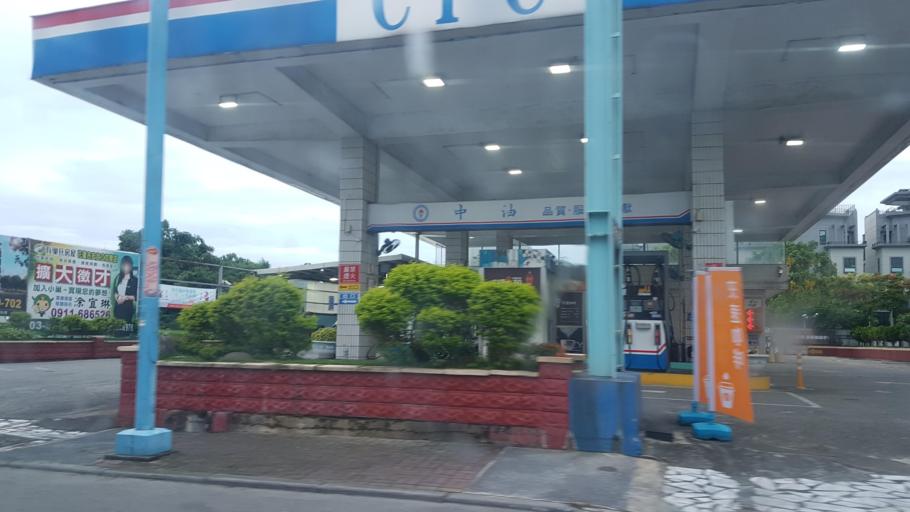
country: TW
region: Taiwan
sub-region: Hualien
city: Hualian
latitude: 23.9815
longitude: 121.5919
